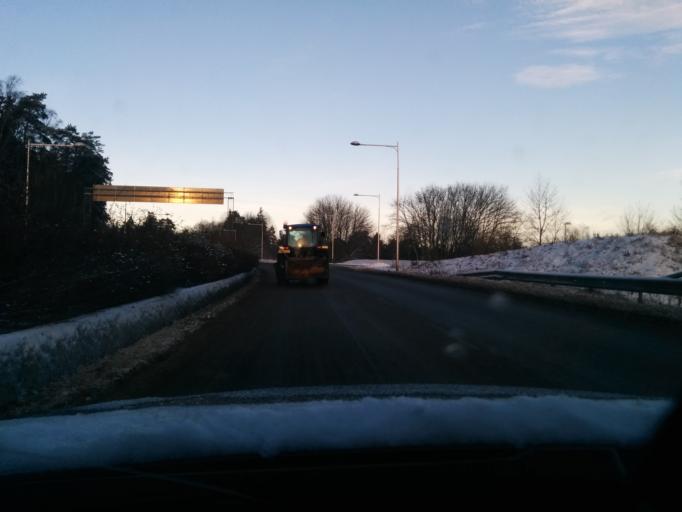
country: SE
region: Stockholm
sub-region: Taby Kommun
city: Taby
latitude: 59.4538
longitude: 18.0866
